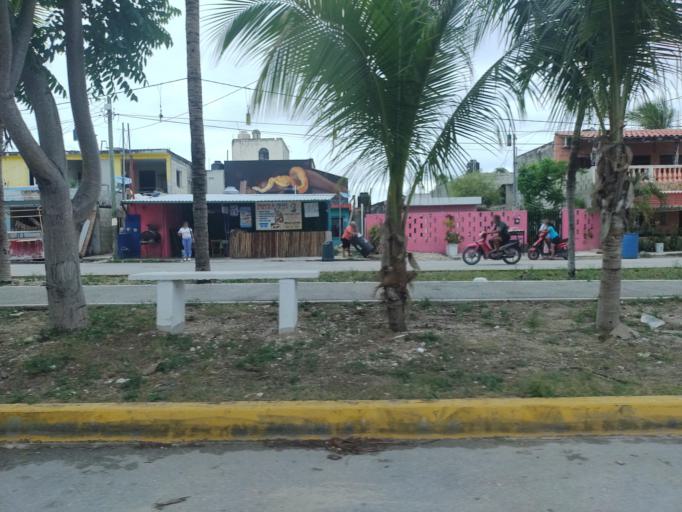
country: MX
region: Quintana Roo
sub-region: Tulum
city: Ciudad Chemuyil
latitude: 20.4012
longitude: -87.3227
